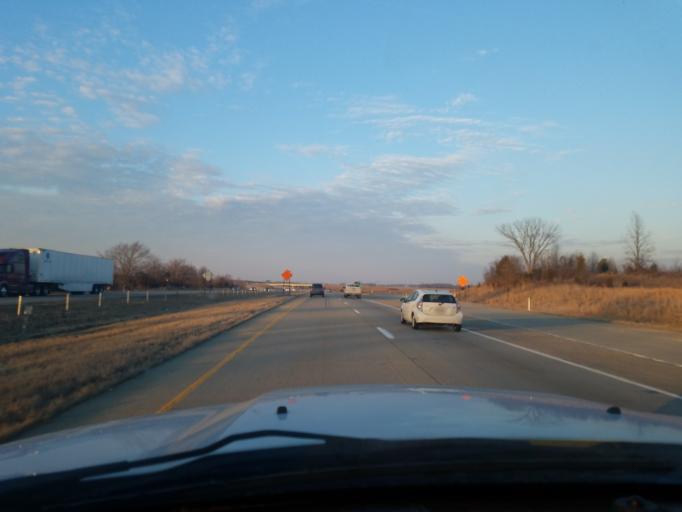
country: US
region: Indiana
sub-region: Vanderburgh County
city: Darmstadt
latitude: 38.1282
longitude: -87.4755
